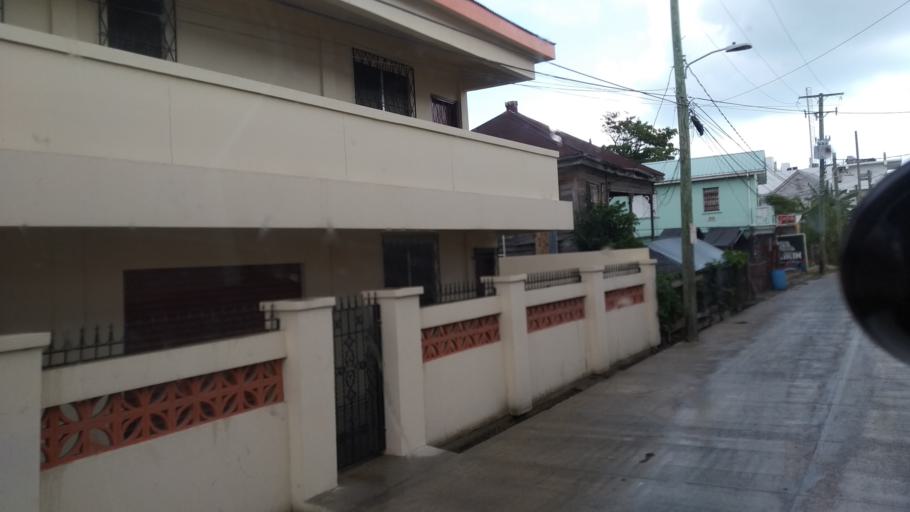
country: BZ
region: Belize
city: Belize City
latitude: 17.4984
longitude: -88.1898
